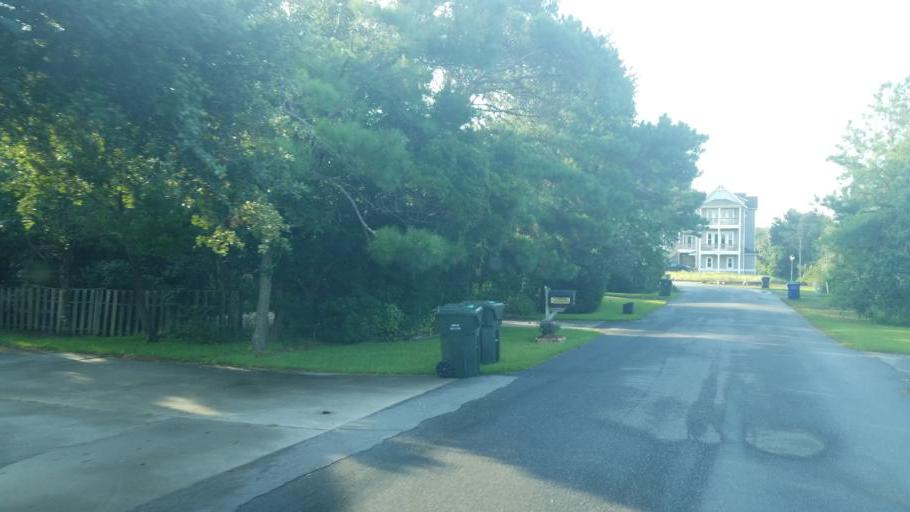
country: US
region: North Carolina
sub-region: Dare County
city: Nags Head
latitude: 35.9736
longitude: -75.6359
